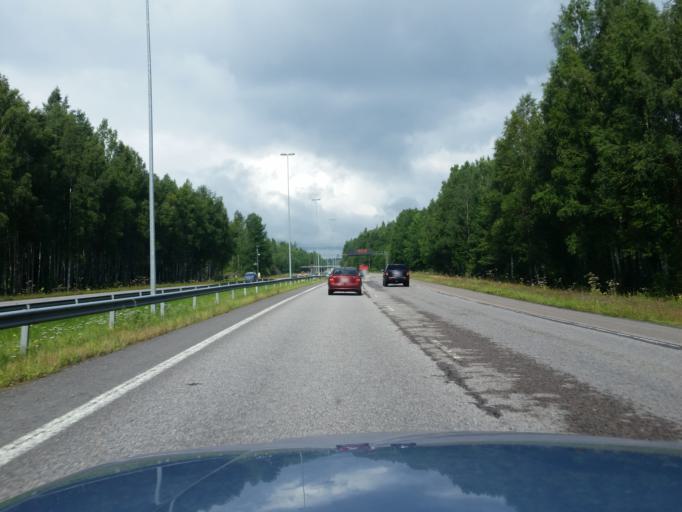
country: FI
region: Uusimaa
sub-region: Helsinki
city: Vihti
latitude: 60.2926
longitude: 24.3224
